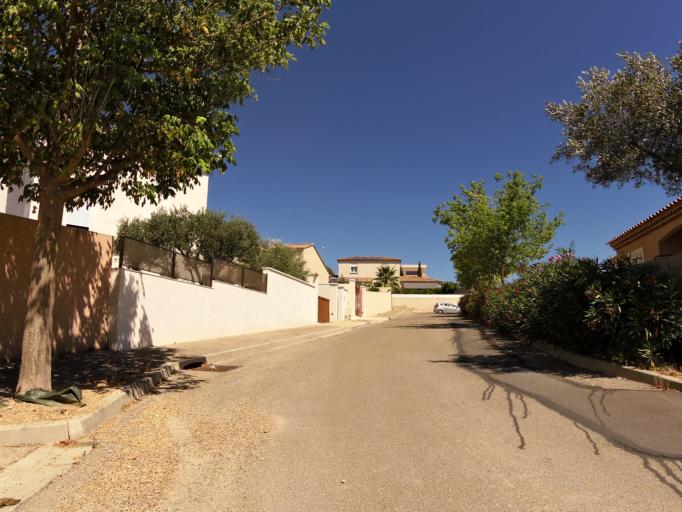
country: FR
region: Languedoc-Roussillon
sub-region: Departement du Gard
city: Vergeze
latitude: 43.7442
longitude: 4.2303
